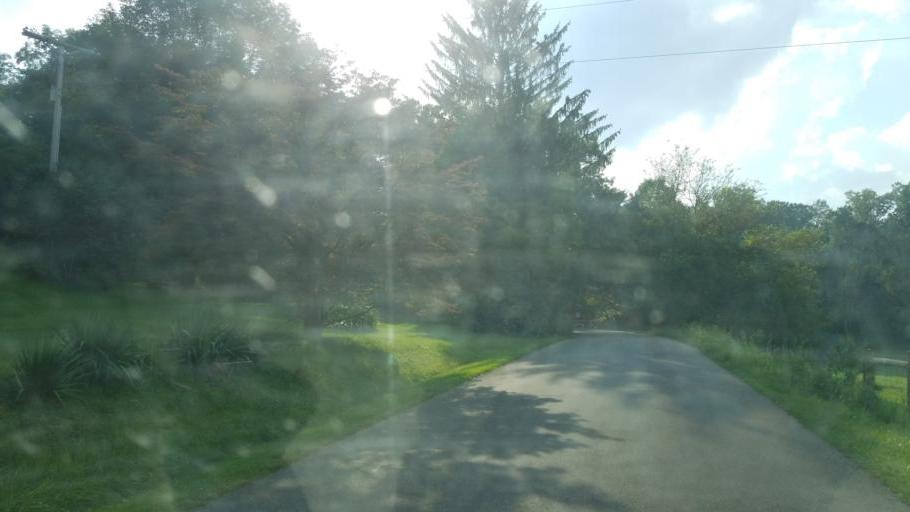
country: US
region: Ohio
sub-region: Knox County
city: Gambier
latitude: 40.3675
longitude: -82.4065
